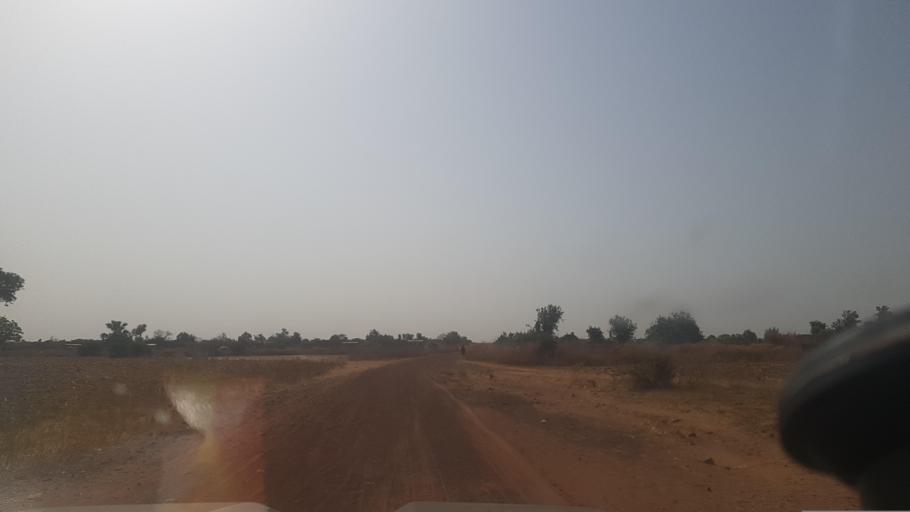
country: ML
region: Segou
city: Baroueli
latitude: 13.1633
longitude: -6.5179
